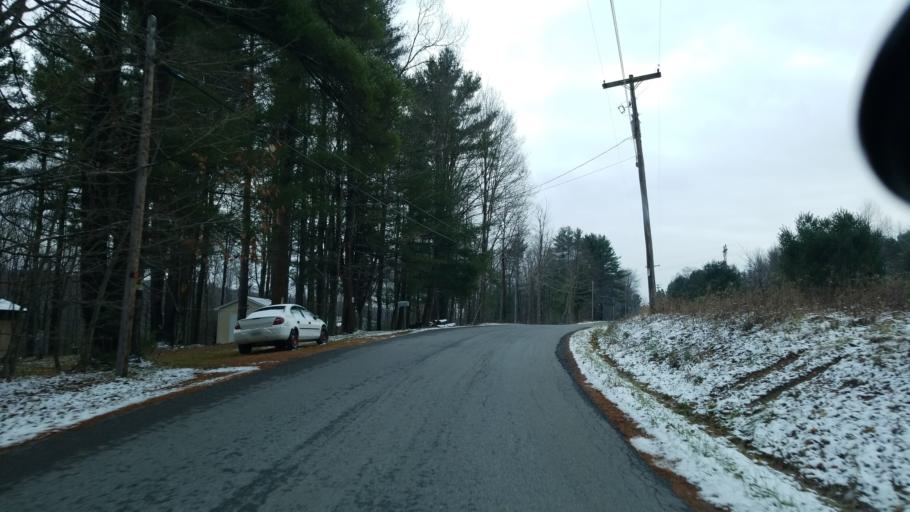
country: US
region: Pennsylvania
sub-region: Clearfield County
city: Treasure Lake
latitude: 41.0852
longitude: -78.6393
